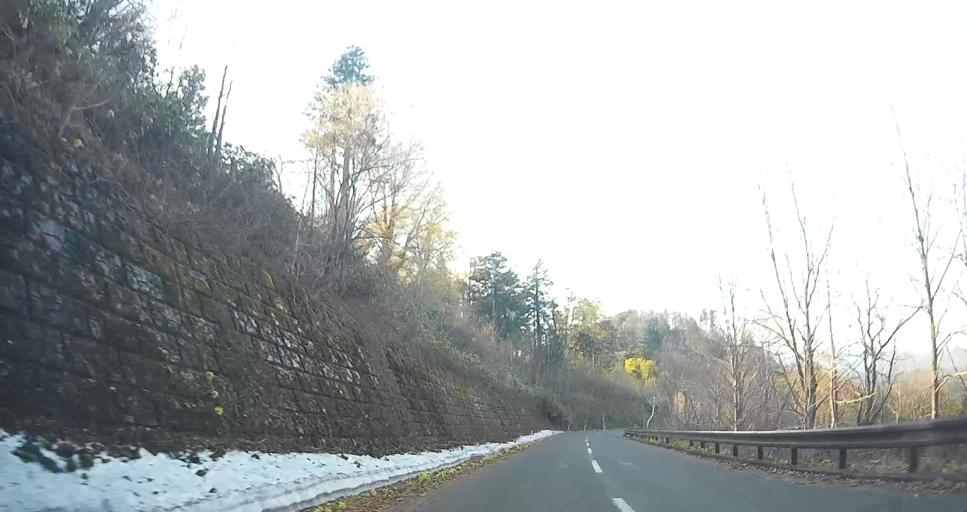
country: JP
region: Aomori
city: Mutsu
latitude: 41.3080
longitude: 141.1143
